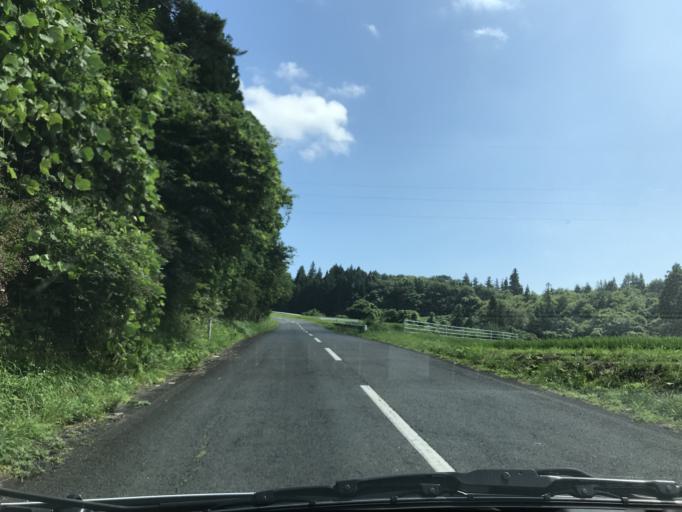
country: JP
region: Iwate
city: Ofunato
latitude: 39.0039
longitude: 141.4252
